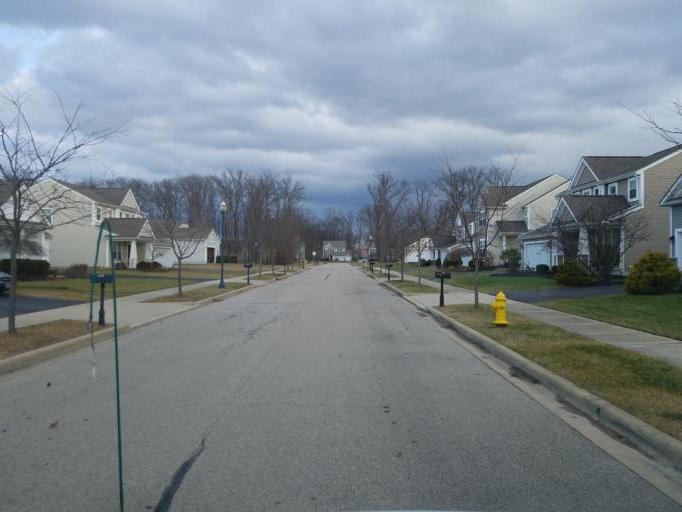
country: US
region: Ohio
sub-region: Delaware County
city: Delaware
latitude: 40.3186
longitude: -83.1058
